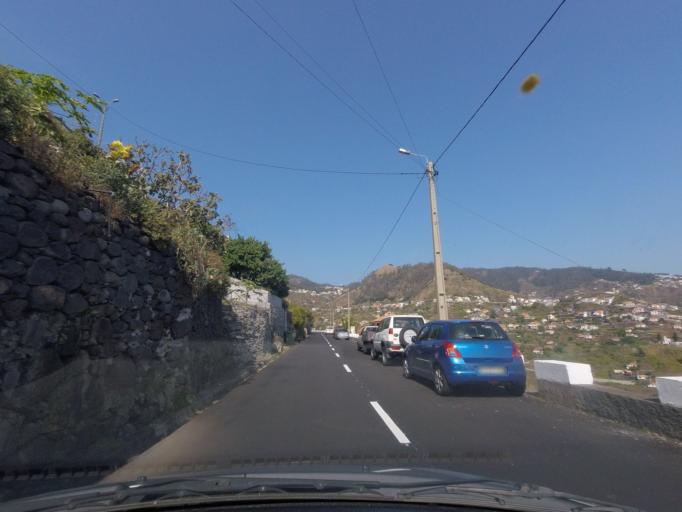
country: PT
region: Madeira
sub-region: Ribeira Brava
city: Campanario
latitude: 32.6684
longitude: -17.0462
